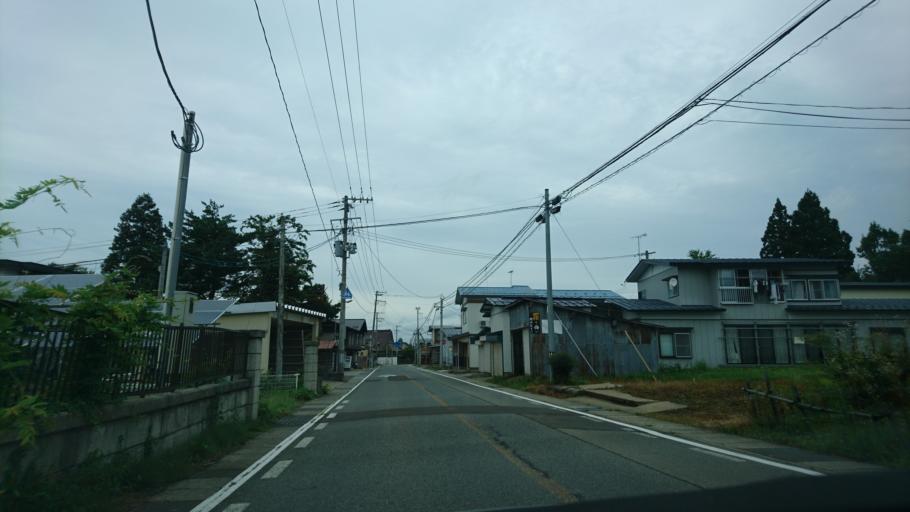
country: JP
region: Akita
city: Yuzawa
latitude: 39.1332
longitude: 140.5752
